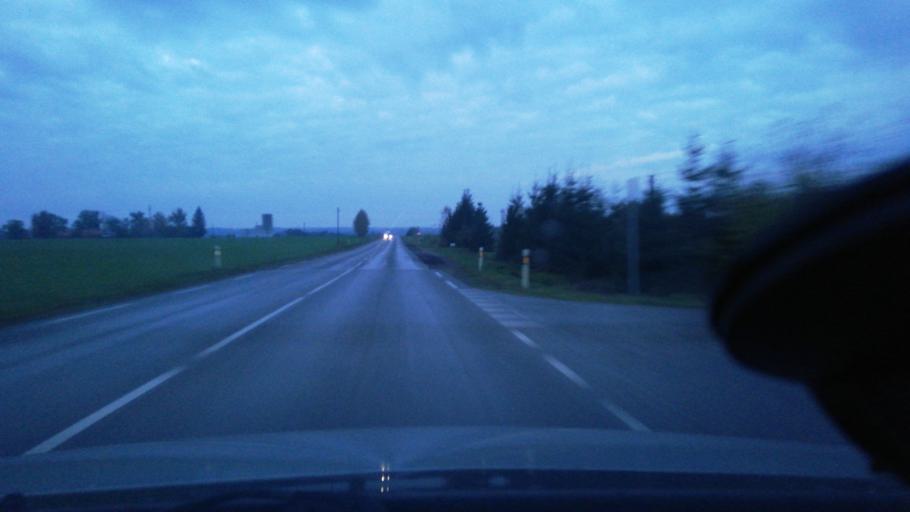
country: LT
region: Telsiu apskritis
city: Plunge
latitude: 55.8864
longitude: 21.7903
